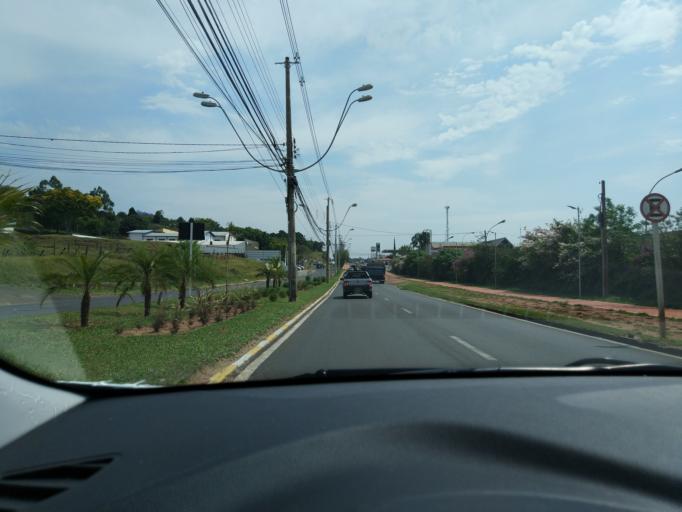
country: BR
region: Sao Paulo
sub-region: Botucatu
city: Botucatu
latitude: -22.8728
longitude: -48.4747
